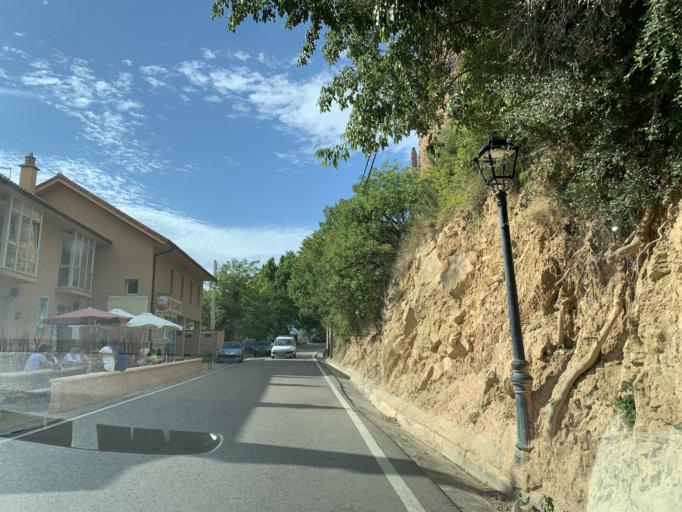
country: ES
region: Aragon
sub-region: Provincia de Zaragoza
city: Santa Eulalia de Gallego
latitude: 42.3469
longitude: -0.7266
